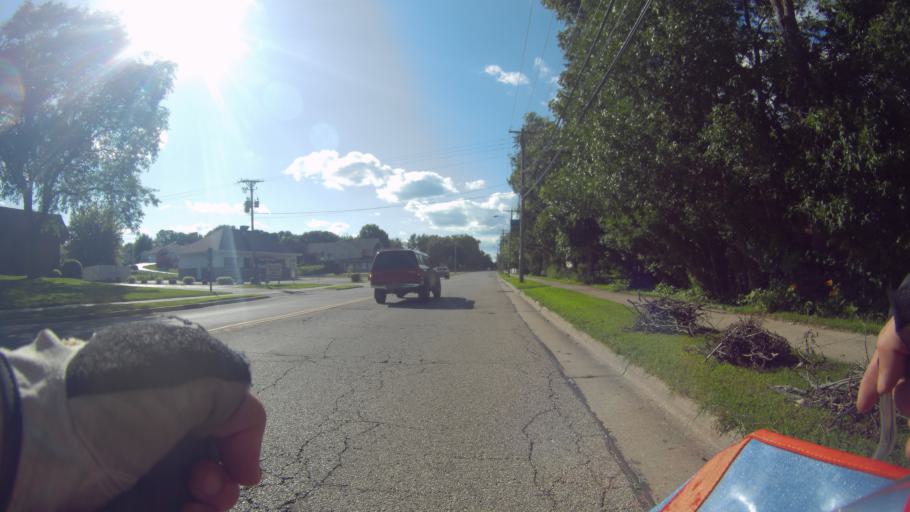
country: US
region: Wisconsin
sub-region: Dane County
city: Oregon
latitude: 42.9198
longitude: -89.3765
